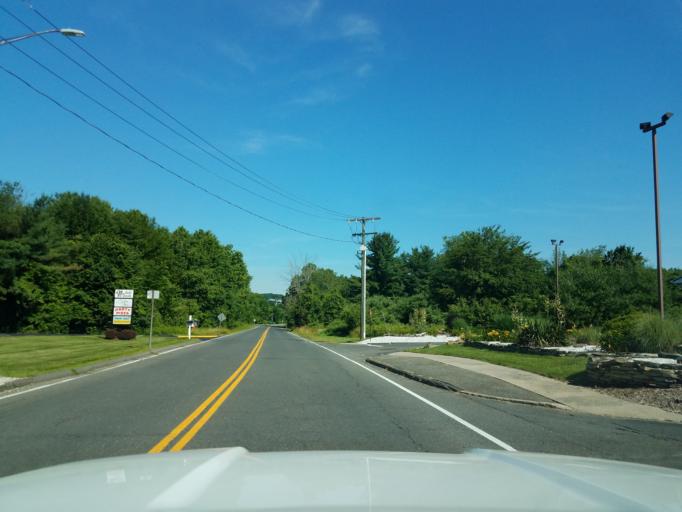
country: US
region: Connecticut
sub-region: Middlesex County
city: Cromwell
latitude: 41.5997
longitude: -72.6778
